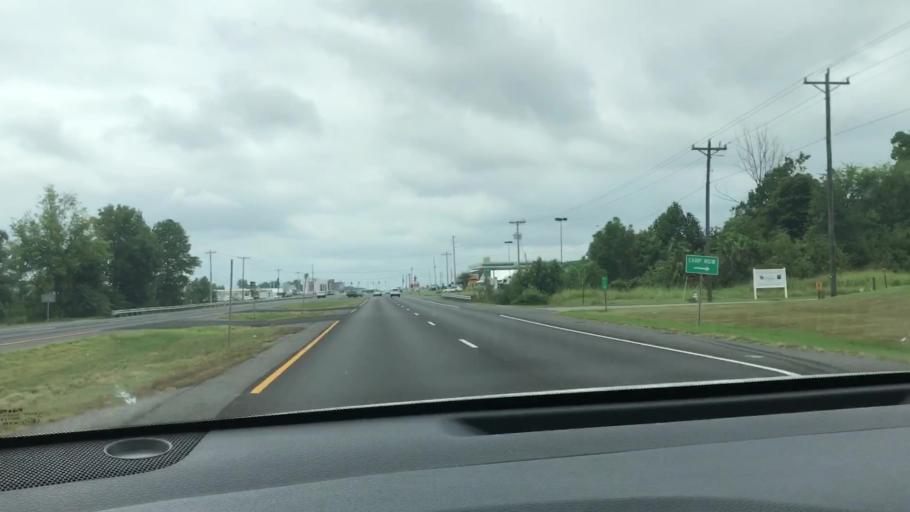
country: US
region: Kentucky
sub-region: Calloway County
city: Murray
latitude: 36.6433
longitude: -88.3086
